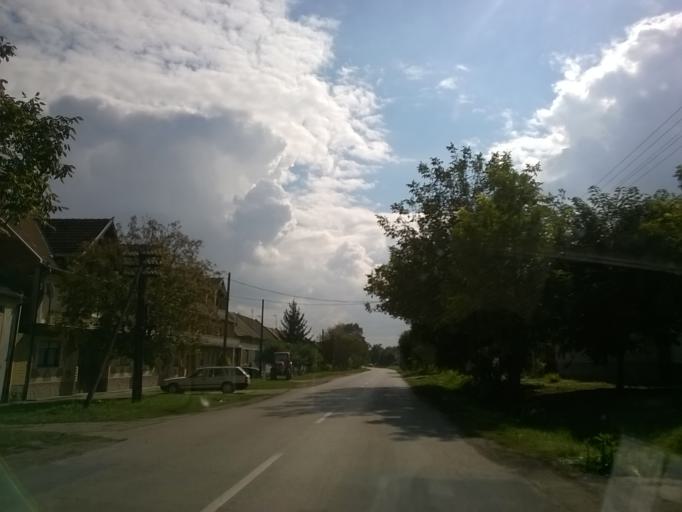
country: RS
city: Seleus
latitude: 45.1287
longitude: 20.9140
